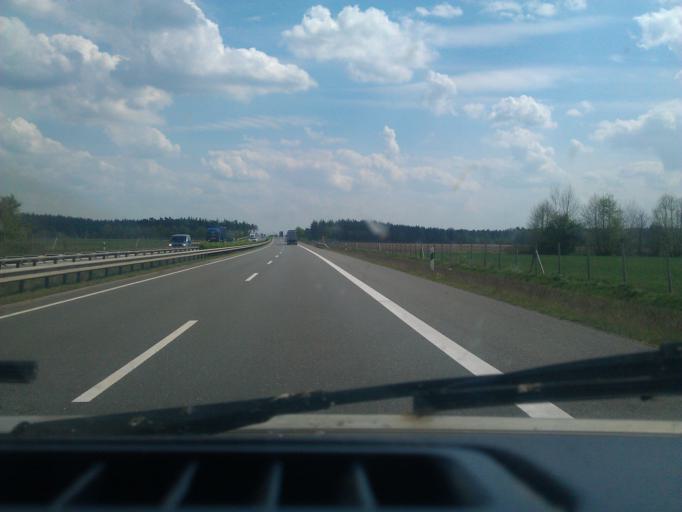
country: DE
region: Lower Saxony
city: Emsburen
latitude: 52.3767
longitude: 7.2478
